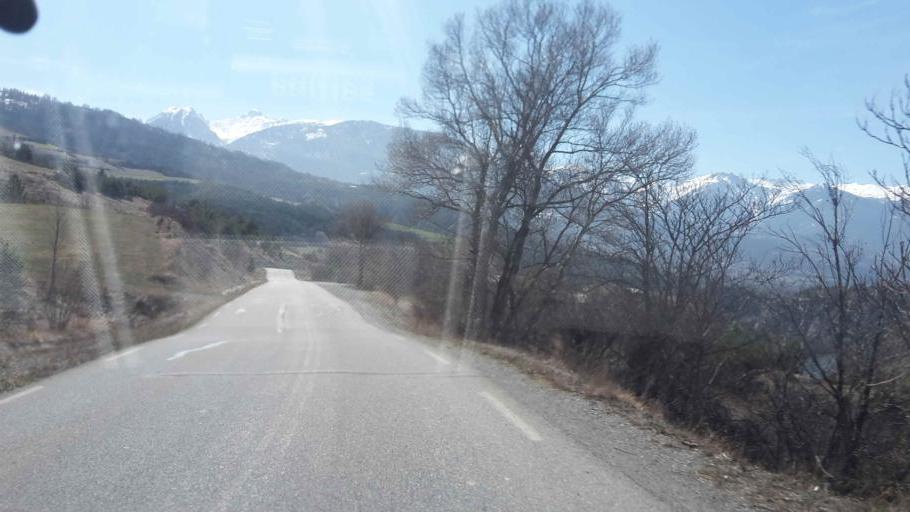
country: FR
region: Provence-Alpes-Cote d'Azur
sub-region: Departement des Hautes-Alpes
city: Embrun
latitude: 44.5720
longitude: 6.5240
